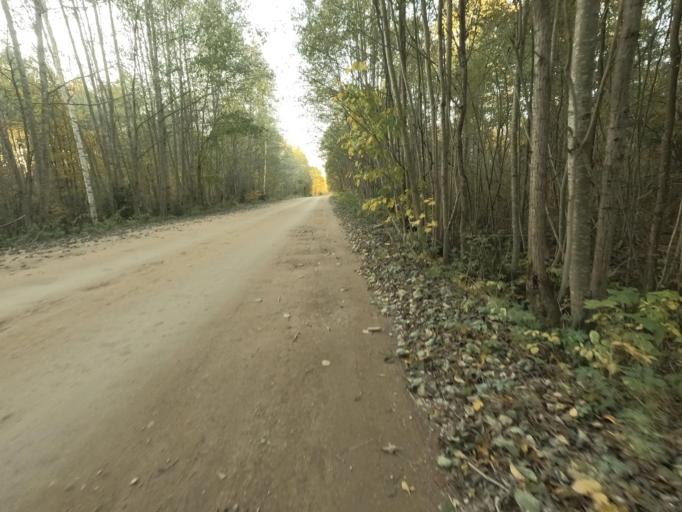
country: RU
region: Leningrad
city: Lyuban'
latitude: 58.9980
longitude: 31.1040
